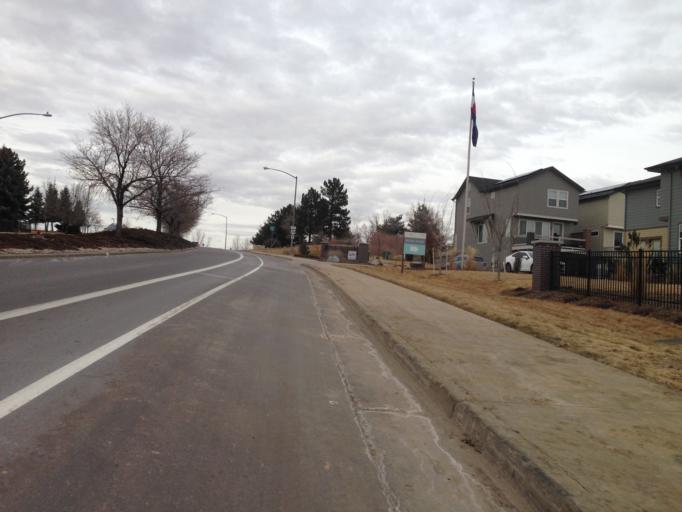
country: US
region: Colorado
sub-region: Adams County
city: Westminster
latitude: 39.8591
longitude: -105.0514
